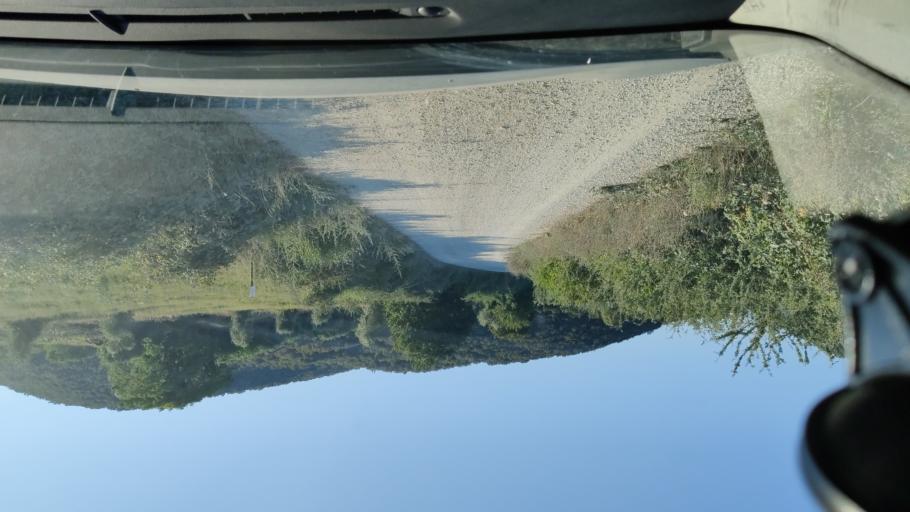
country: IT
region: Umbria
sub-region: Provincia di Terni
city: Amelia
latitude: 42.5434
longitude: 12.3868
